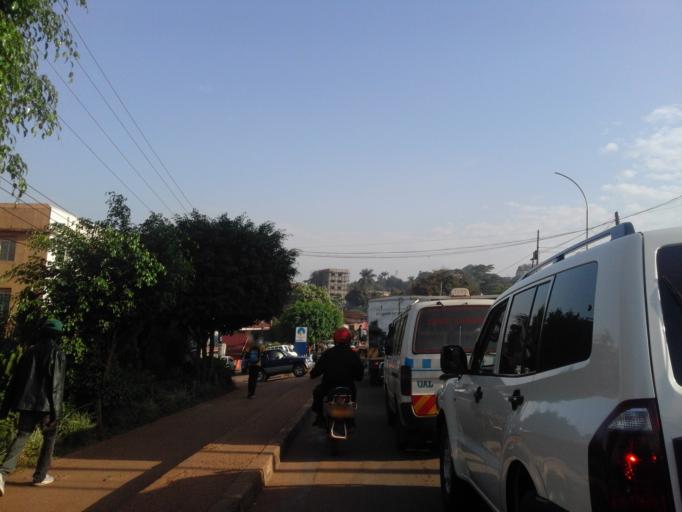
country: UG
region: Central Region
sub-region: Kampala District
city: Kampala
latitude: 0.2958
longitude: 32.6050
